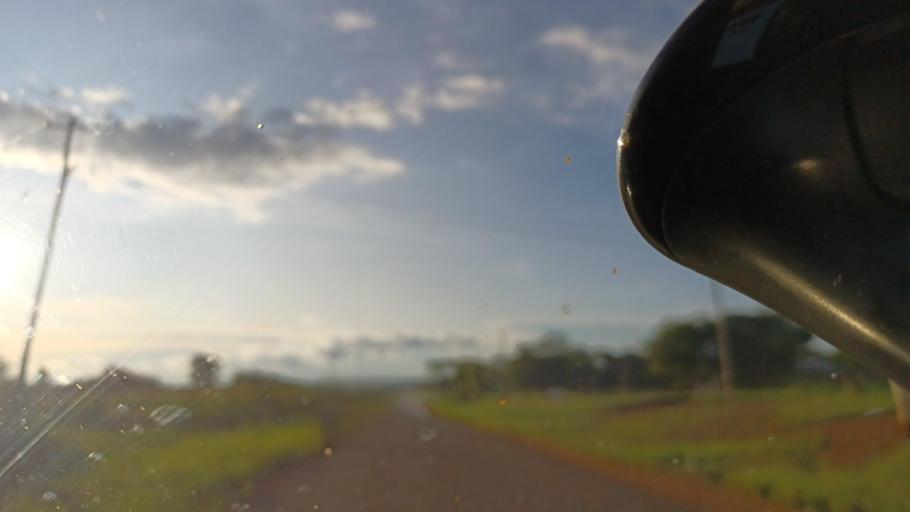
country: ZM
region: North-Western
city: Kasempa
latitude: -13.4663
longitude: 25.8583
